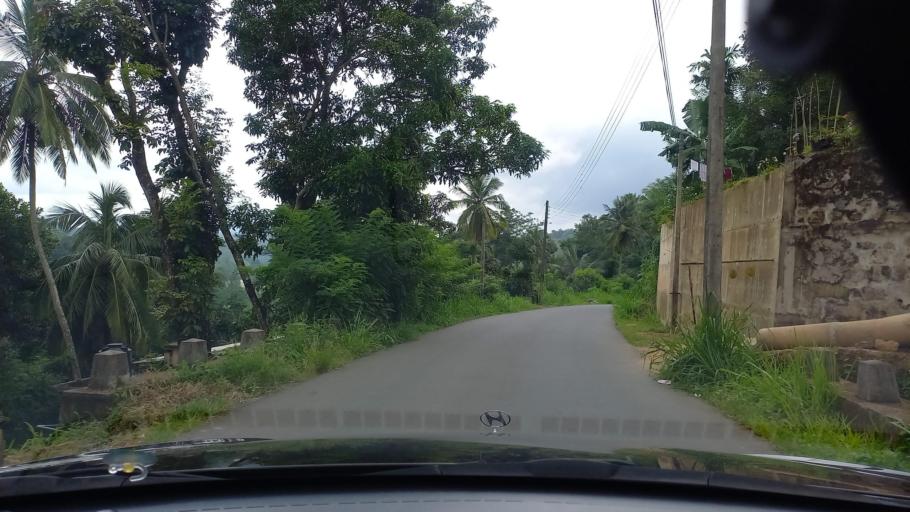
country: LK
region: Central
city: Gampola
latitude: 7.2092
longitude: 80.6231
